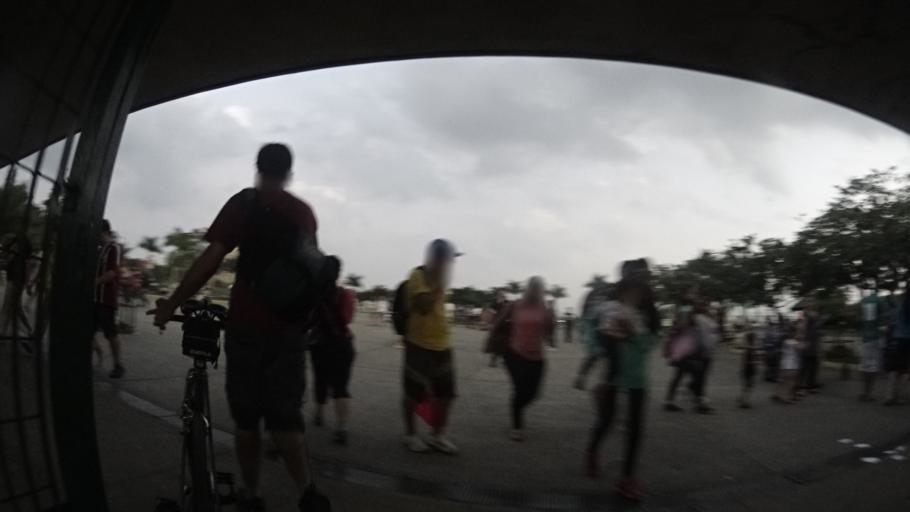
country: BR
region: Sao Paulo
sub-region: Osasco
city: Osasco
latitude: -23.5440
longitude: -46.7262
